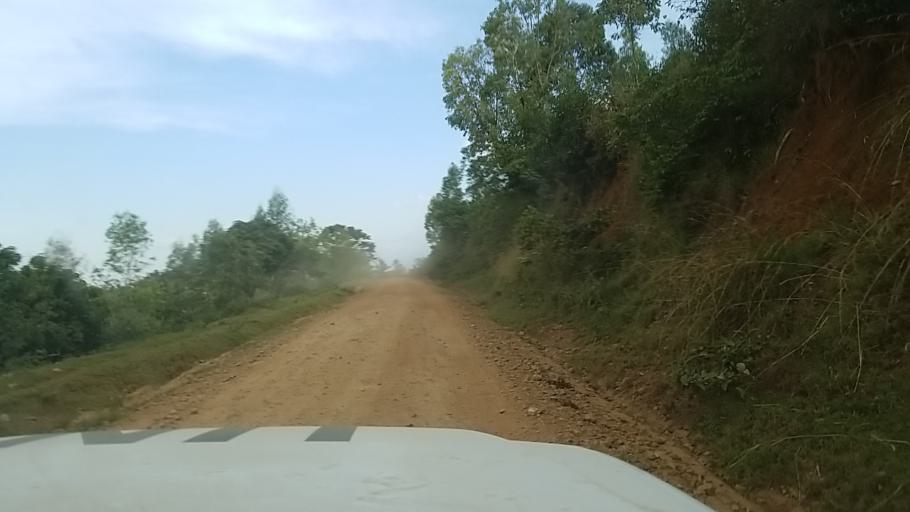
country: RW
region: Western Province
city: Cyangugu
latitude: -2.1103
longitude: 28.9021
